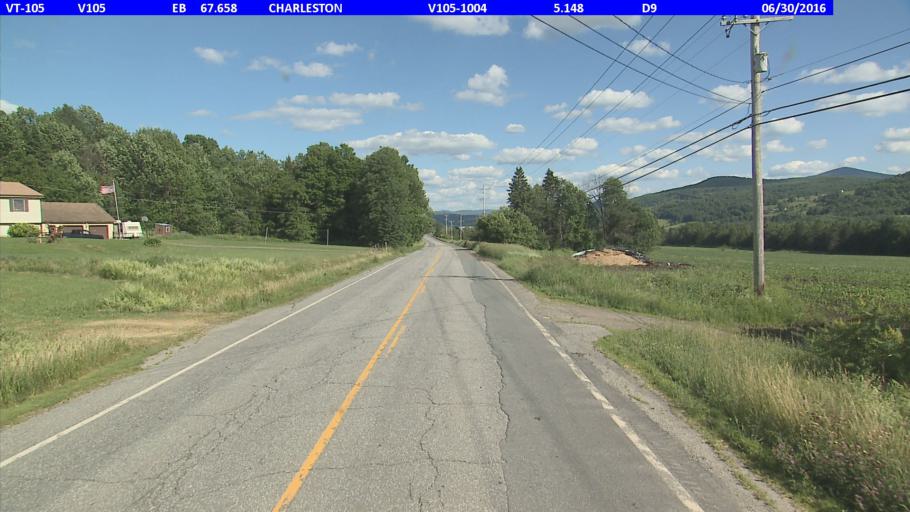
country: US
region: Vermont
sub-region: Orleans County
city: Newport
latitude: 44.8496
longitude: -72.0246
